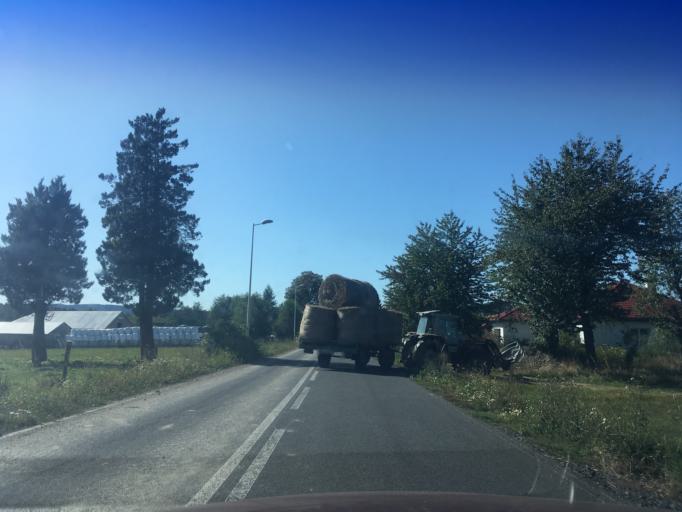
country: PL
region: Lower Silesian Voivodeship
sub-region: Powiat lubanski
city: Lesna
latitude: 50.9742
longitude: 15.3005
